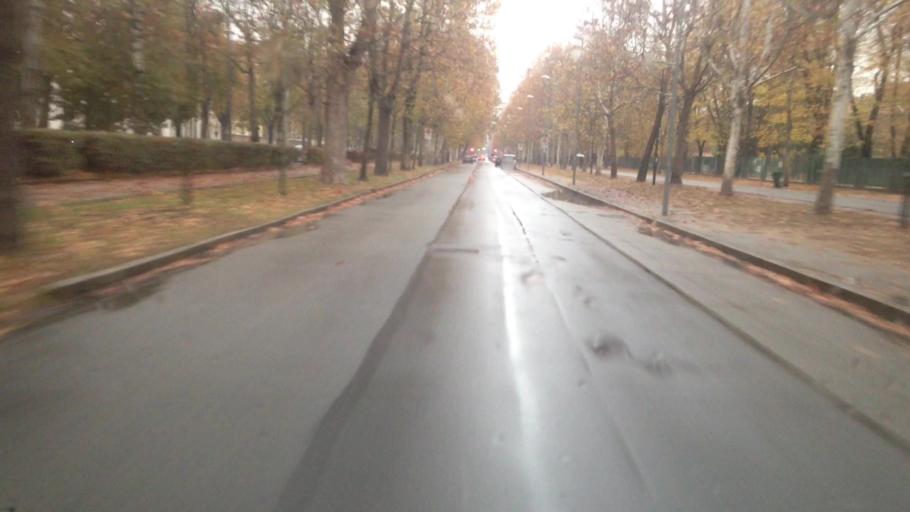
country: IT
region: Piedmont
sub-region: Provincia di Torino
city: Lesna
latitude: 45.0461
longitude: 7.6514
